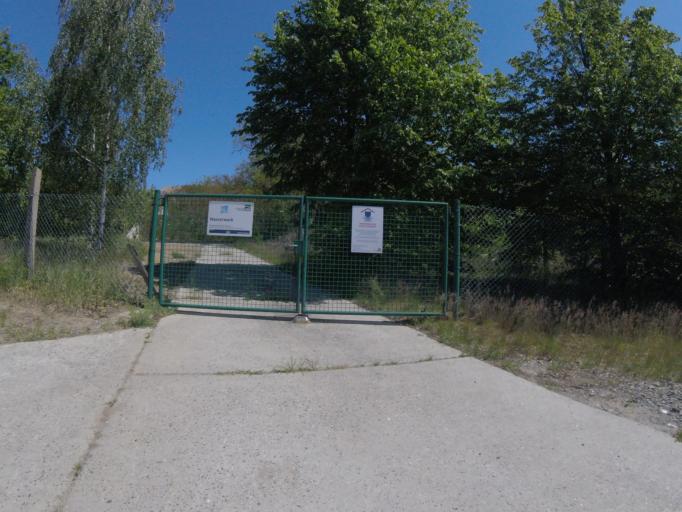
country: DE
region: Brandenburg
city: Teupitz
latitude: 52.1309
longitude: 13.6137
